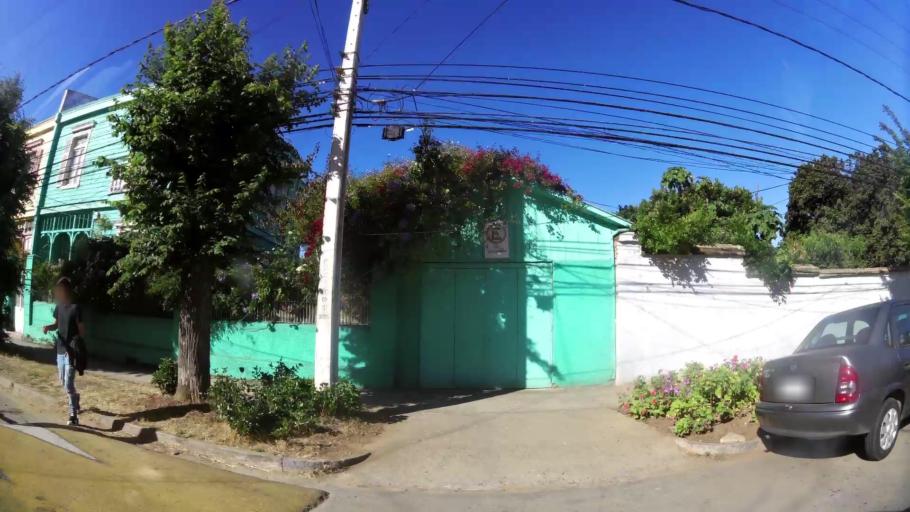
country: CL
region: Valparaiso
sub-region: Provincia de Valparaiso
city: Vina del Mar
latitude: -33.0293
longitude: -71.5624
